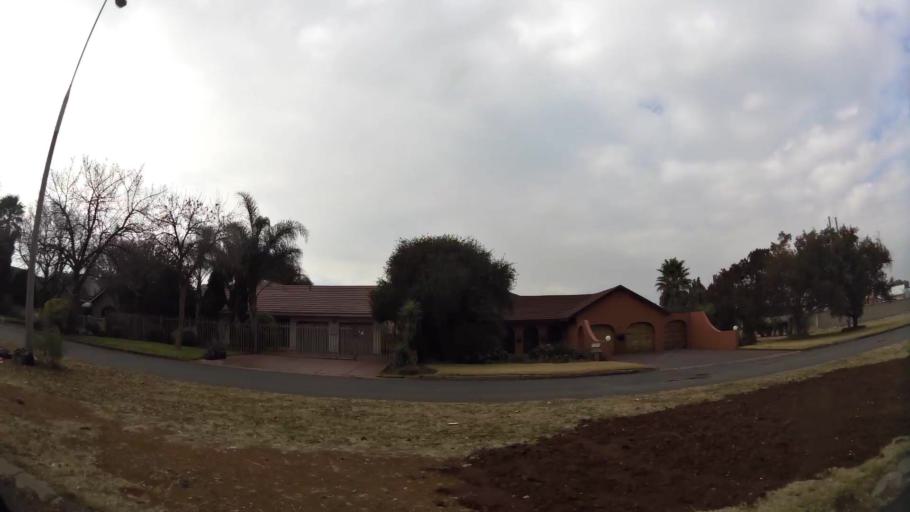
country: ZA
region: Gauteng
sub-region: Sedibeng District Municipality
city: Vanderbijlpark
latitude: -26.6999
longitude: 27.8476
